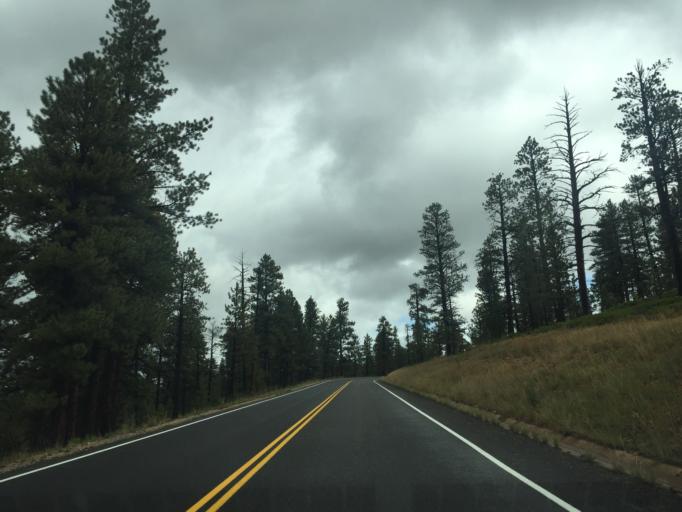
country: US
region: Utah
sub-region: Garfield County
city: Panguitch
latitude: 37.6041
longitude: -112.2063
